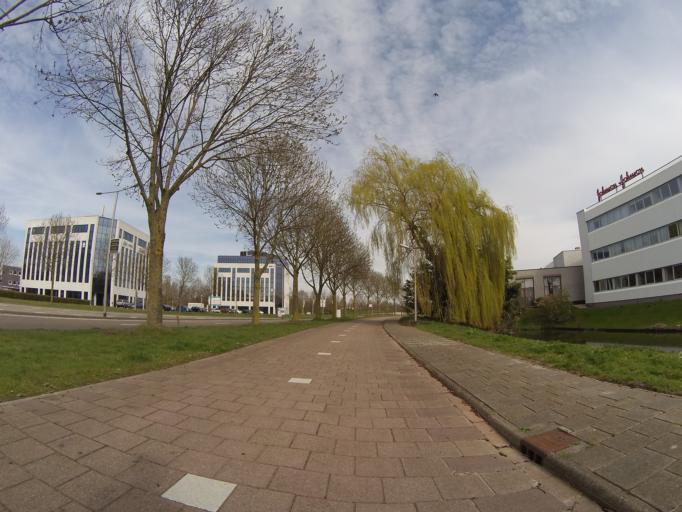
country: NL
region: Utrecht
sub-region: Gemeente Amersfoort
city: Randenbroek
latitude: 52.1765
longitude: 5.4117
